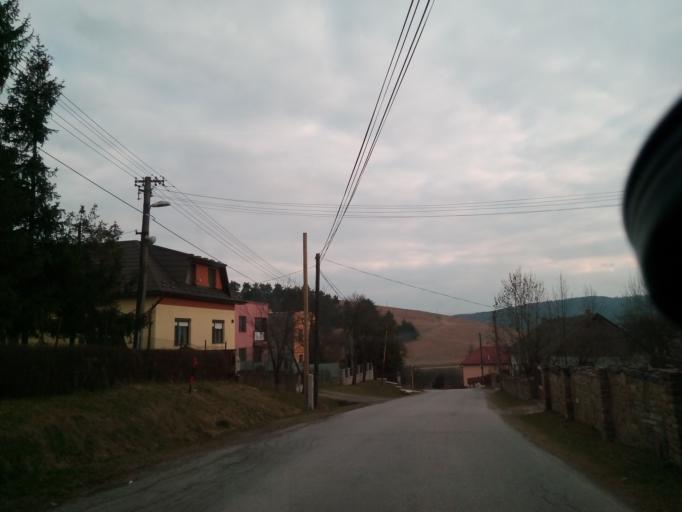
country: SK
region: Presovsky
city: Sabinov
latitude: 49.0451
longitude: 21.0201
